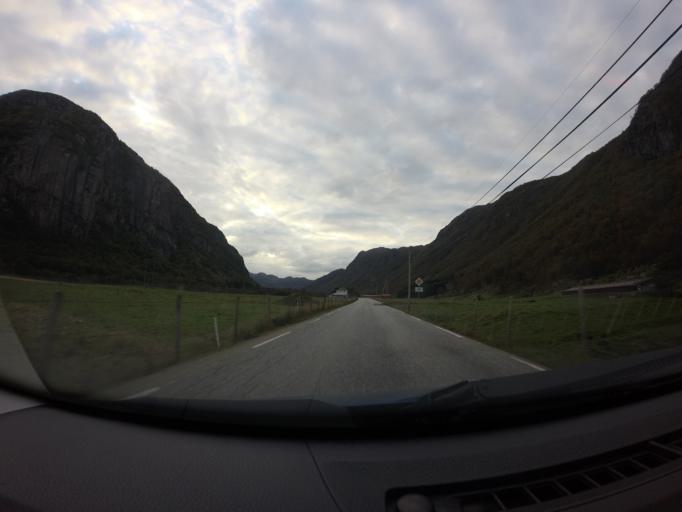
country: NO
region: Rogaland
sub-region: Forsand
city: Forsand
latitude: 58.8254
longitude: 6.1922
